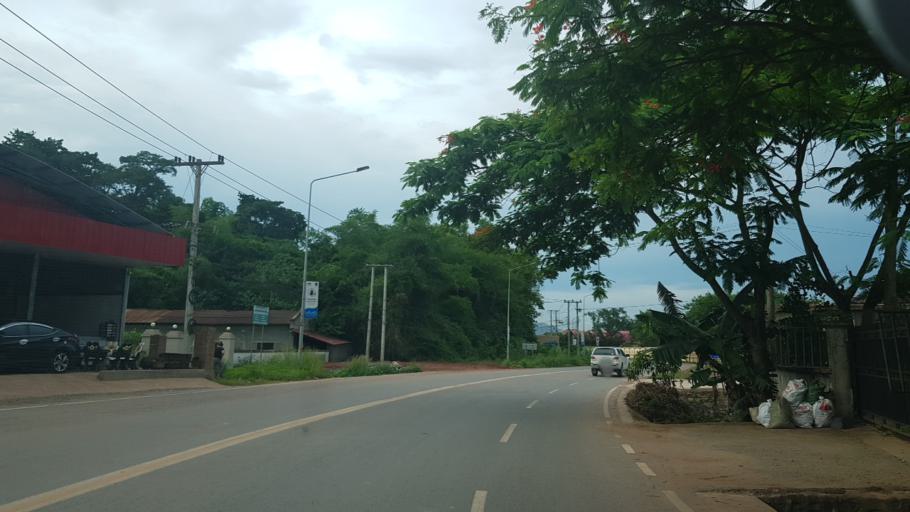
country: LA
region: Oudomxai
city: Muang Xay
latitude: 20.6710
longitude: 101.9832
